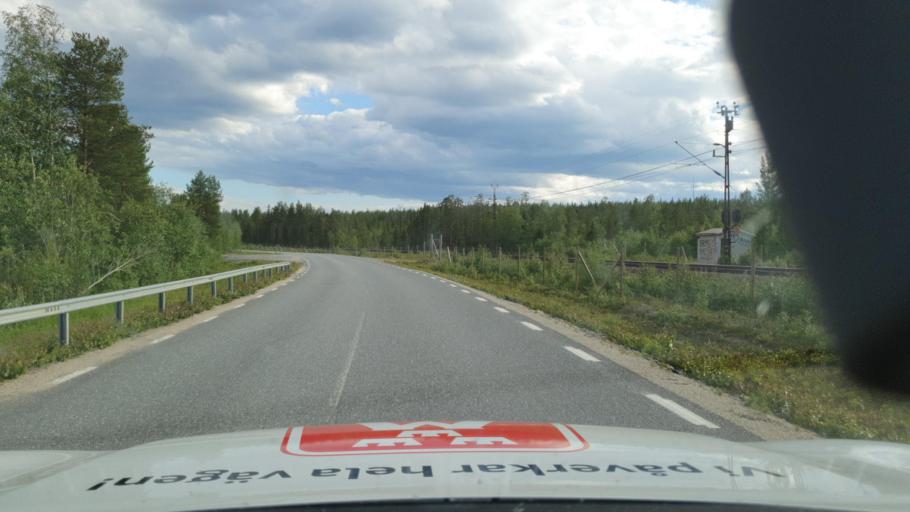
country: SE
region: Vaesterbotten
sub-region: Vindelns Kommun
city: Vindeln
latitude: 64.4534
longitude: 19.7472
